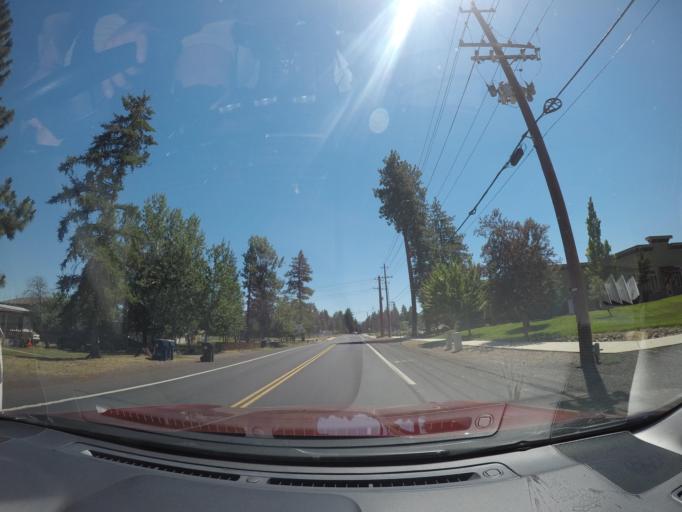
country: US
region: Oregon
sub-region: Deschutes County
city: Sisters
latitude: 44.2921
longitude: -121.5437
